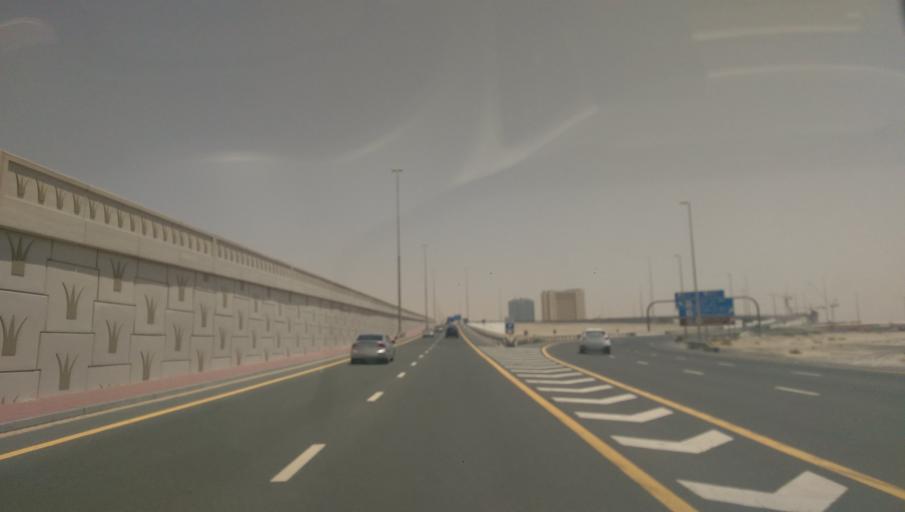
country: AE
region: Dubai
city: Dubai
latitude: 25.0476
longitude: 55.1966
